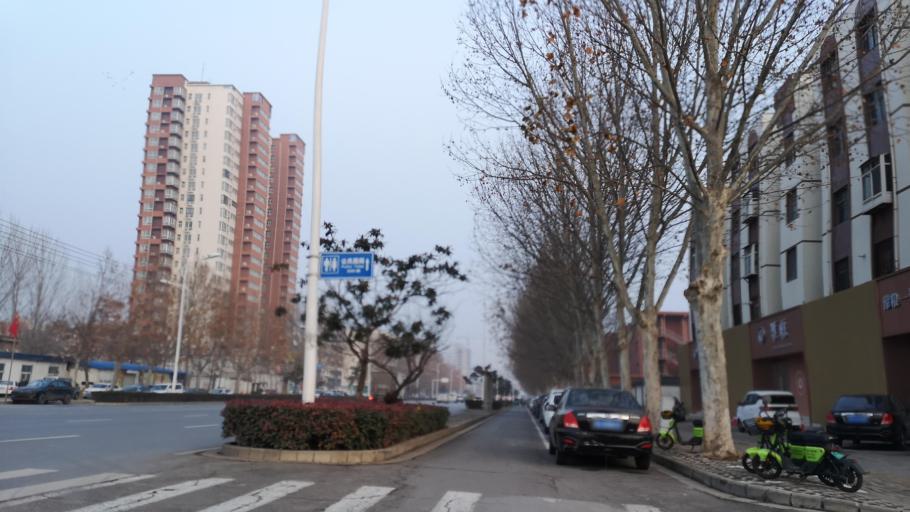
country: CN
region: Henan Sheng
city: Puyang
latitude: 35.7486
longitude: 115.0356
